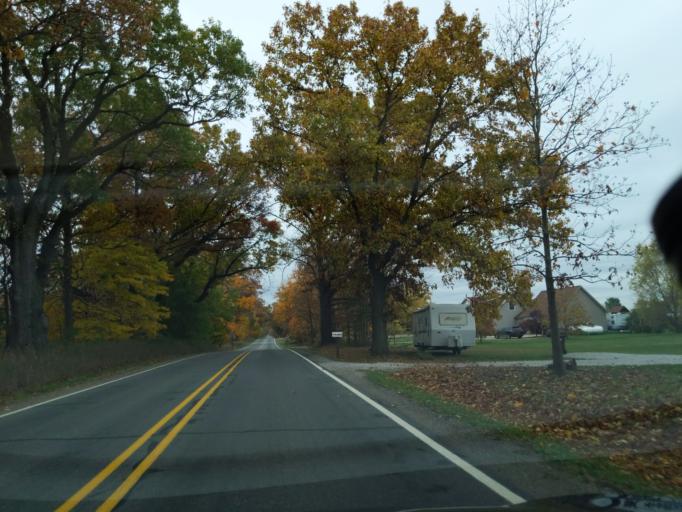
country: US
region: Michigan
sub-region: Jackson County
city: Spring Arbor
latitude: 42.2979
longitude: -84.6002
